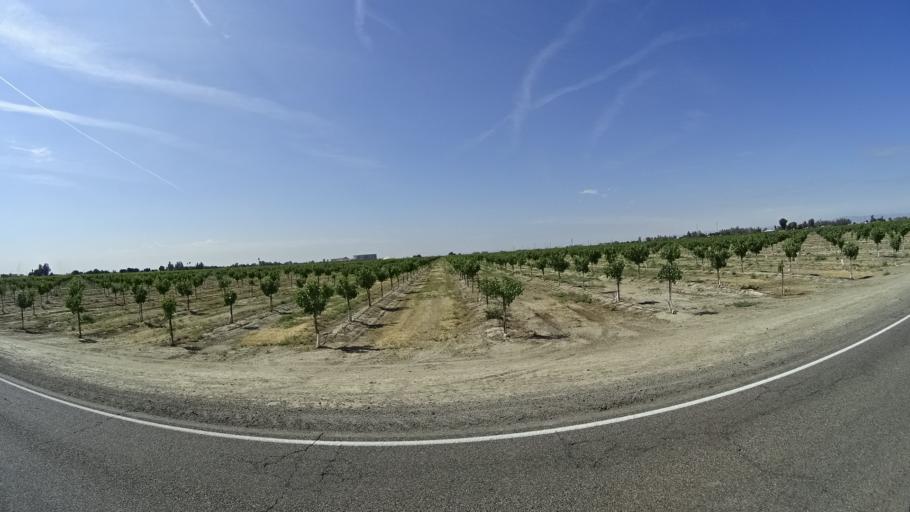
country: US
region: California
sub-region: Kings County
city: Lemoore
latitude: 36.2547
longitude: -119.7702
